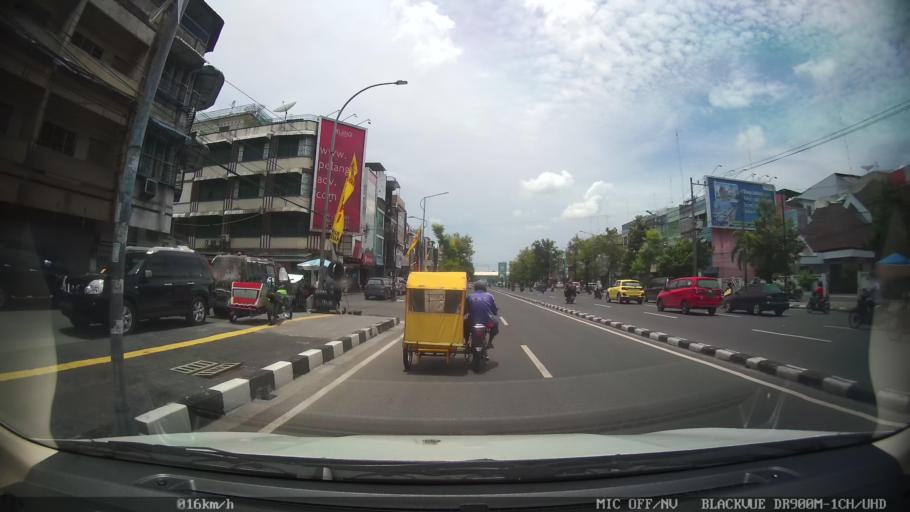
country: ID
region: North Sumatra
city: Medan
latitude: 3.5928
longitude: 98.6675
